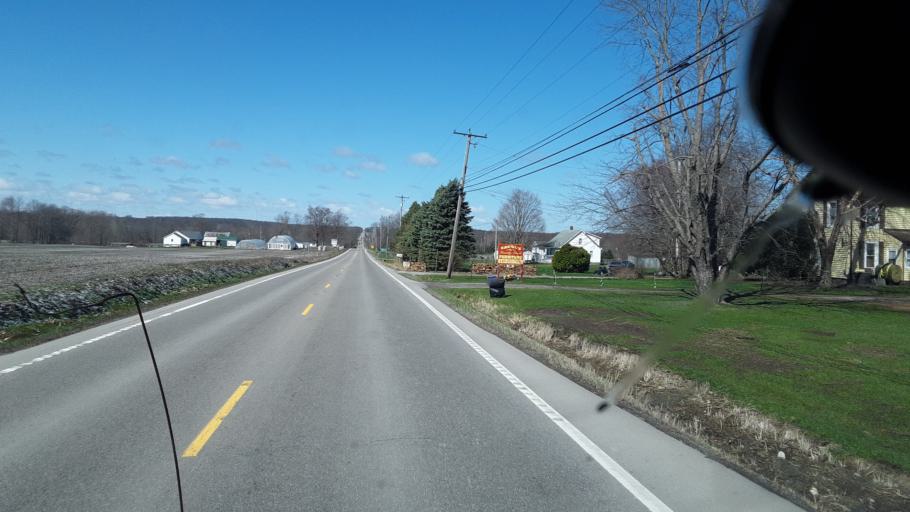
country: US
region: Ohio
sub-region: Ashtabula County
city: Andover
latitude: 41.6070
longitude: -80.6186
